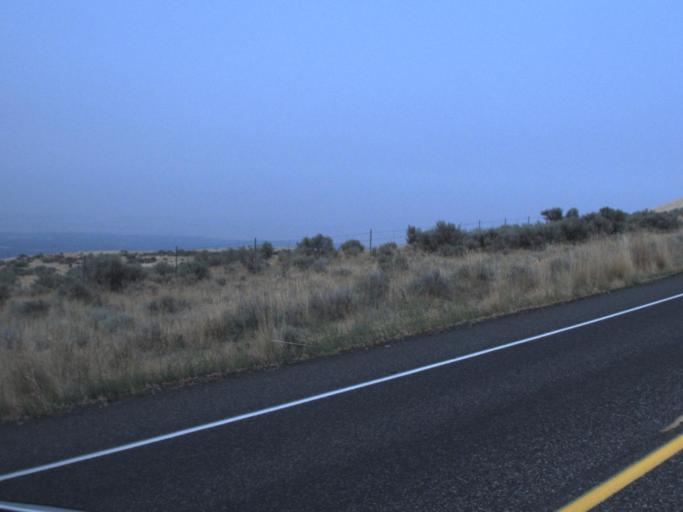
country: US
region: Washington
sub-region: Benton County
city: Prosser
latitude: 46.2004
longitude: -119.7129
